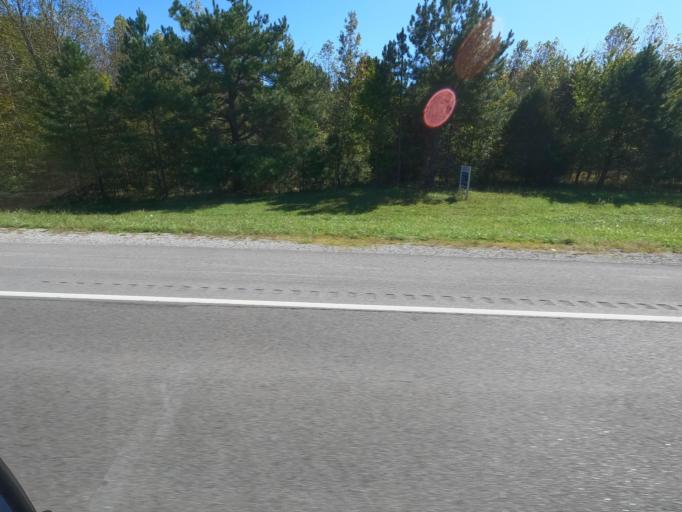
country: US
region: Tennessee
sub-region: Maury County
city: Mount Pleasant
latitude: 35.4480
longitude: -87.2702
